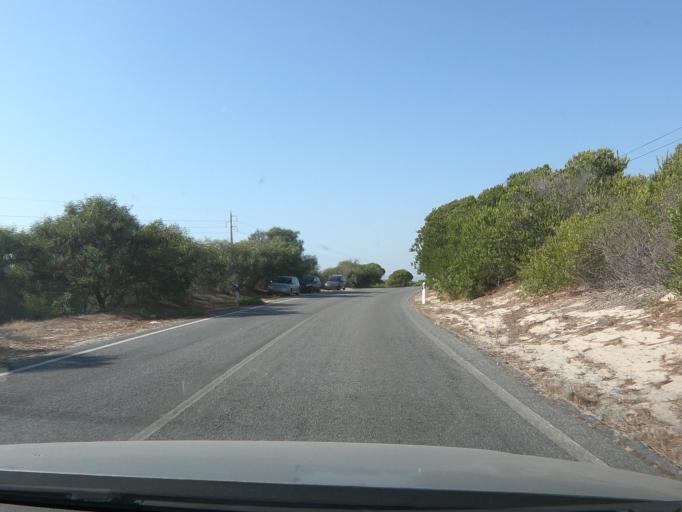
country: PT
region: Setubal
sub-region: Setubal
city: Setubal
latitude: 38.3914
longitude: -8.8021
